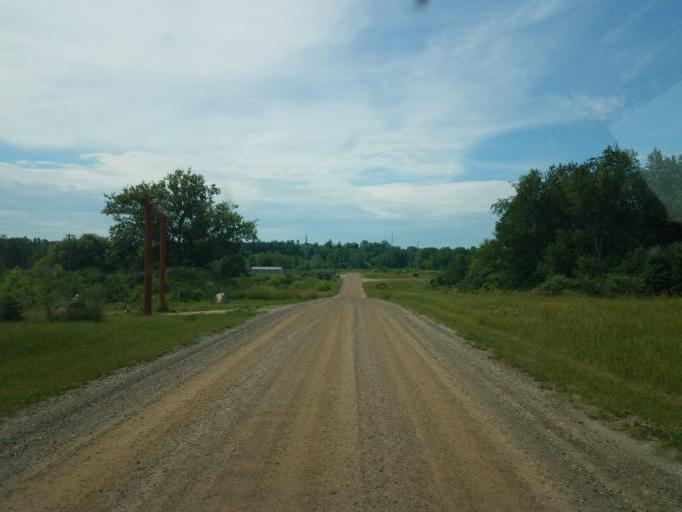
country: US
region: Michigan
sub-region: Eaton County
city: Charlotte
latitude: 42.5870
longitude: -84.8223
